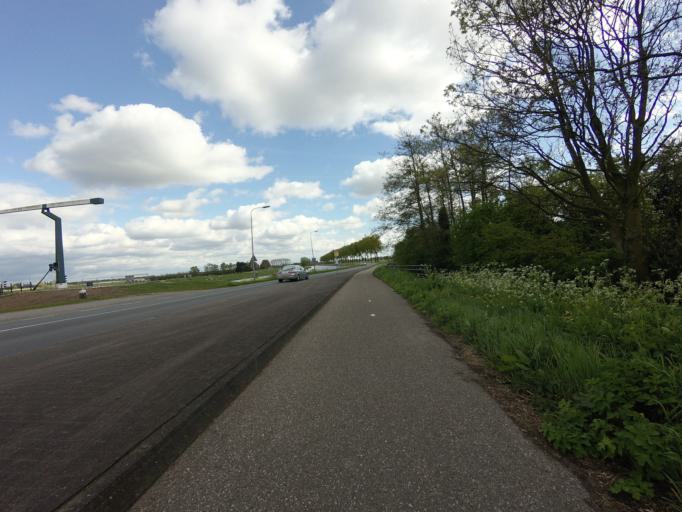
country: NL
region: Utrecht
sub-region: Stichtse Vecht
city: Vreeland
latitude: 52.2432
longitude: 5.0474
